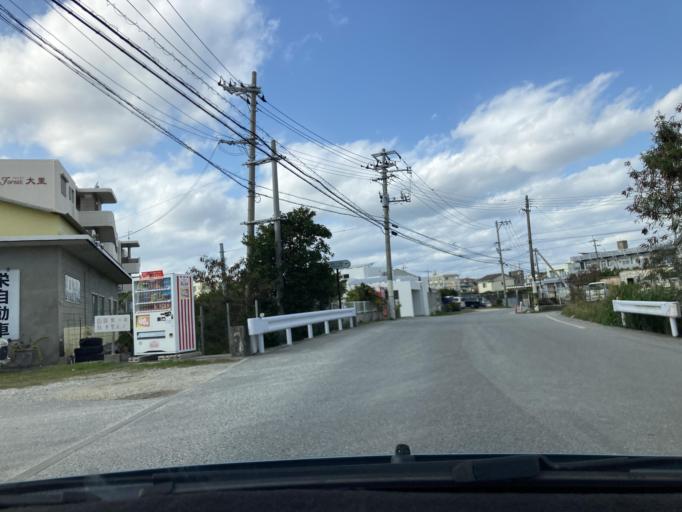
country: JP
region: Okinawa
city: Tomigusuku
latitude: 26.1943
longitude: 127.7484
